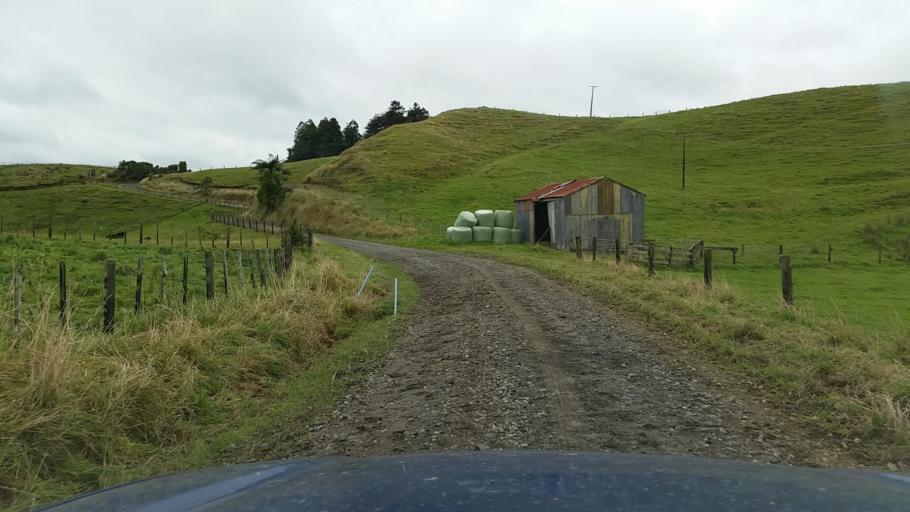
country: NZ
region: Taranaki
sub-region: South Taranaki District
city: Eltham
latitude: -39.2793
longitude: 174.3384
